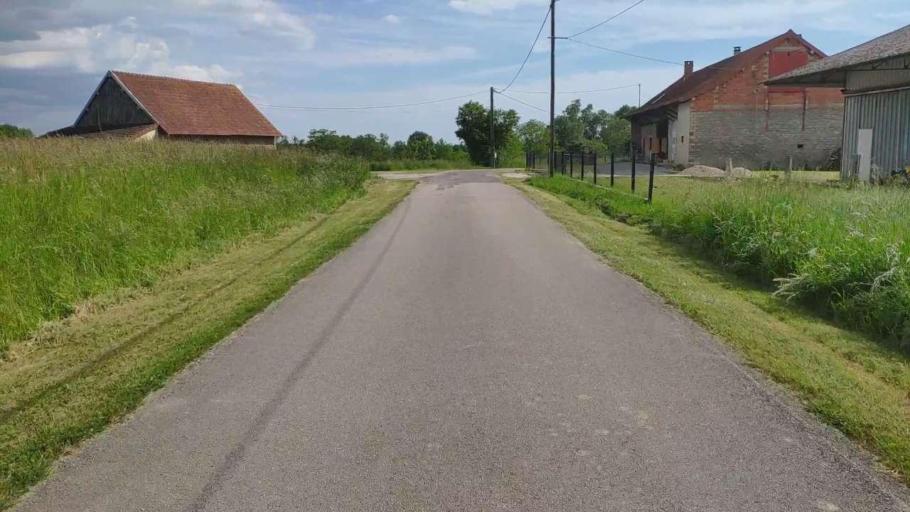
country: FR
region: Franche-Comte
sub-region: Departement du Jura
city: Bletterans
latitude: 46.8142
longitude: 5.3794
